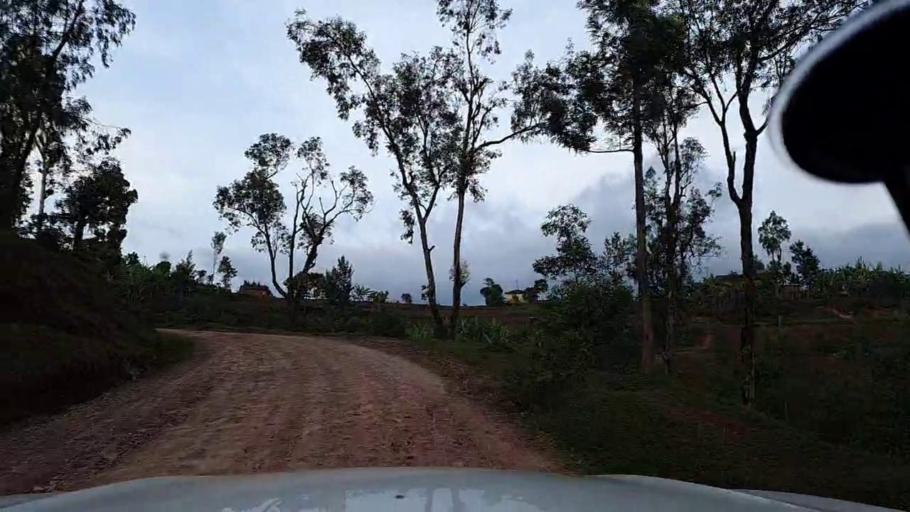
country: RW
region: Southern Province
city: Gitarama
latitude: -2.2082
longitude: 29.6038
